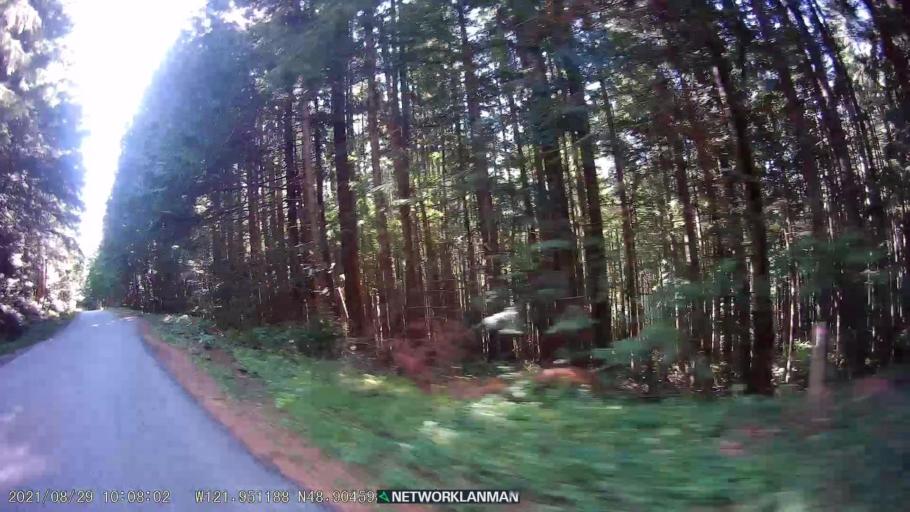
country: US
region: Washington
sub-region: Whatcom County
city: Peaceful Valley
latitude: 48.9032
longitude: -121.9508
